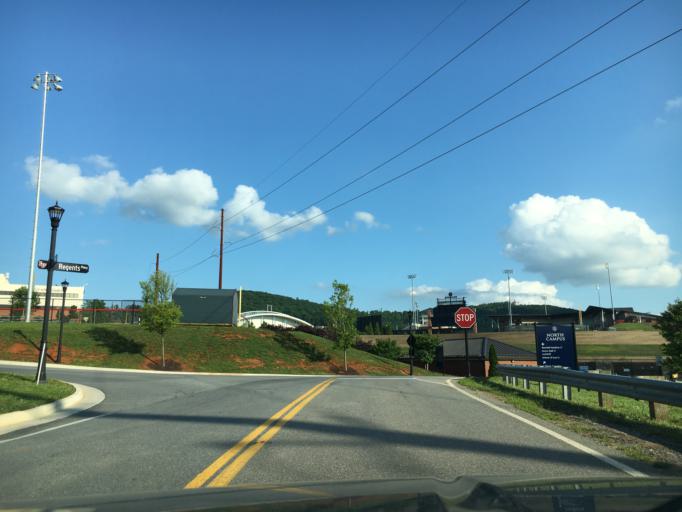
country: US
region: Virginia
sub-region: City of Lynchburg
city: West Lynchburg
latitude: 37.3592
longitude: -79.1780
